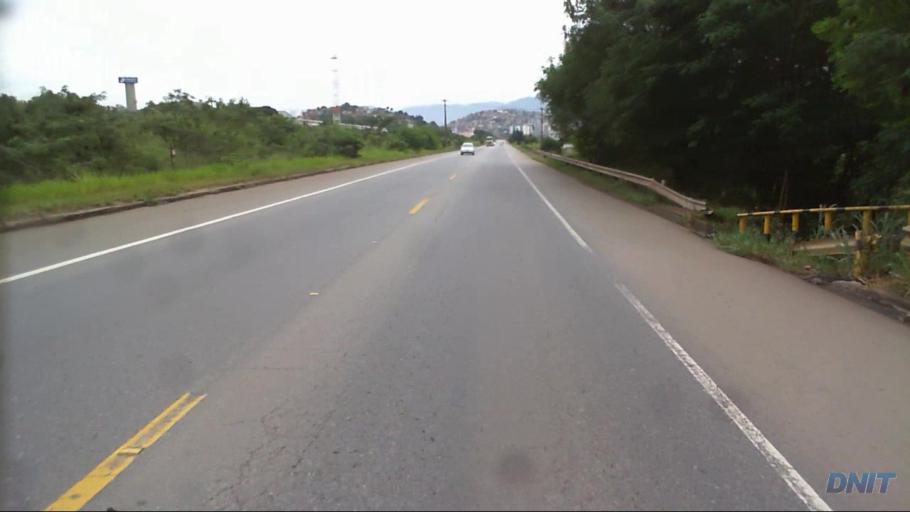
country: BR
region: Minas Gerais
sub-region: Coronel Fabriciano
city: Coronel Fabriciano
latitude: -19.5310
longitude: -42.6062
